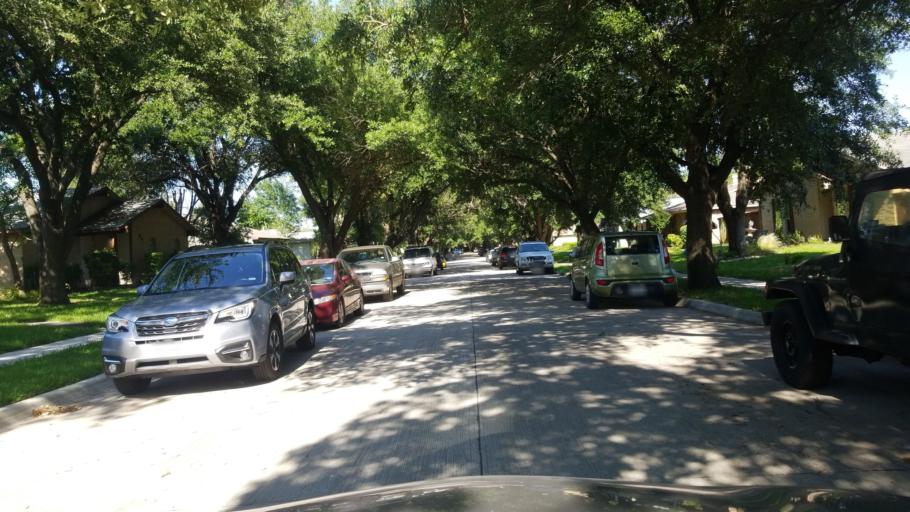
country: US
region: Texas
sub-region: Dallas County
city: Grand Prairie
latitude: 32.6841
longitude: -97.0168
